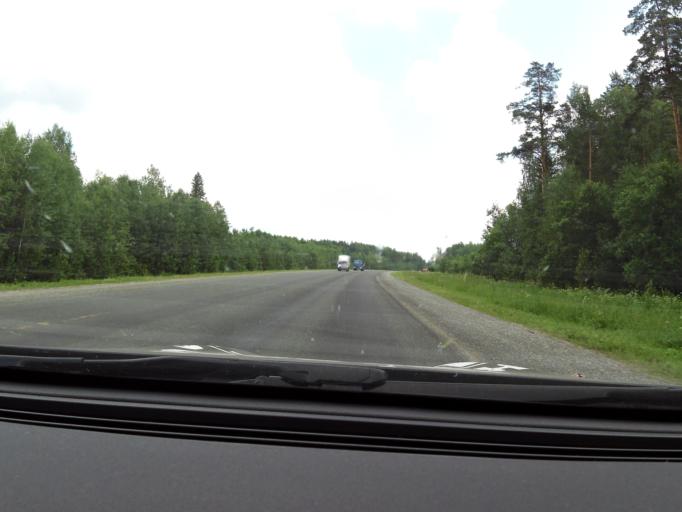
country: RU
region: Sverdlovsk
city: Achit
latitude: 56.7815
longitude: 57.9732
